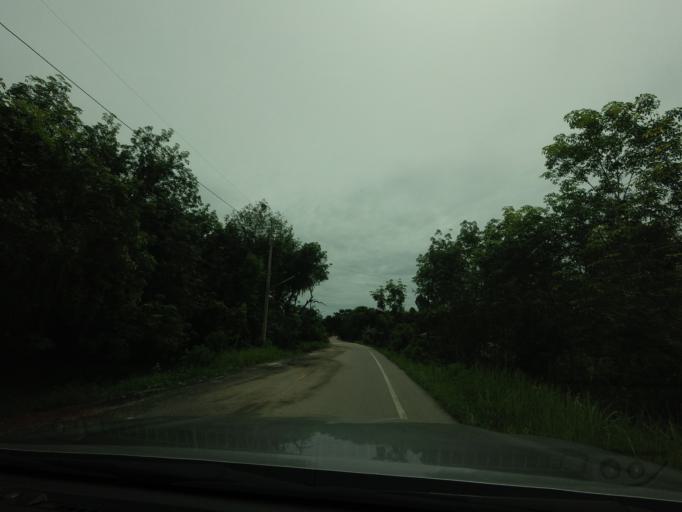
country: TH
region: Pattani
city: Sai Buri
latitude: 6.6613
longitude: 101.5518
